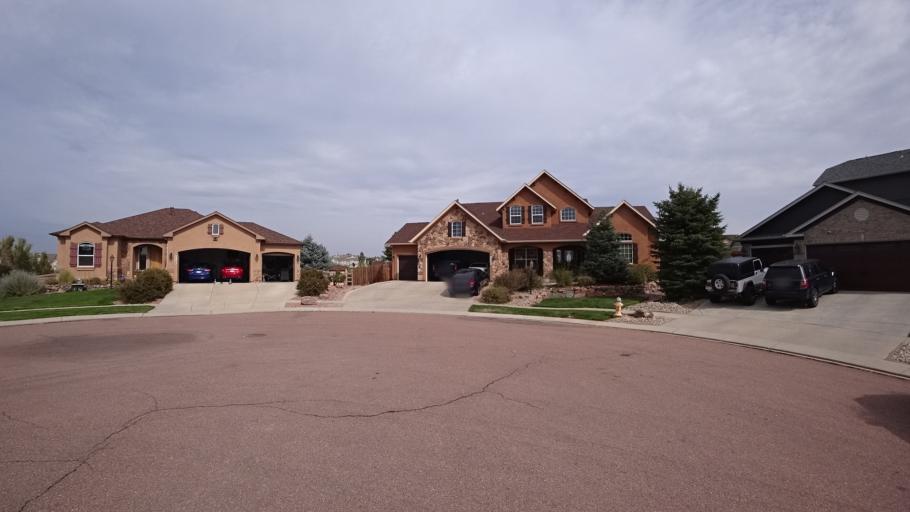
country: US
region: Colorado
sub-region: El Paso County
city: Cimarron Hills
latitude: 38.9230
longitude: -104.6953
